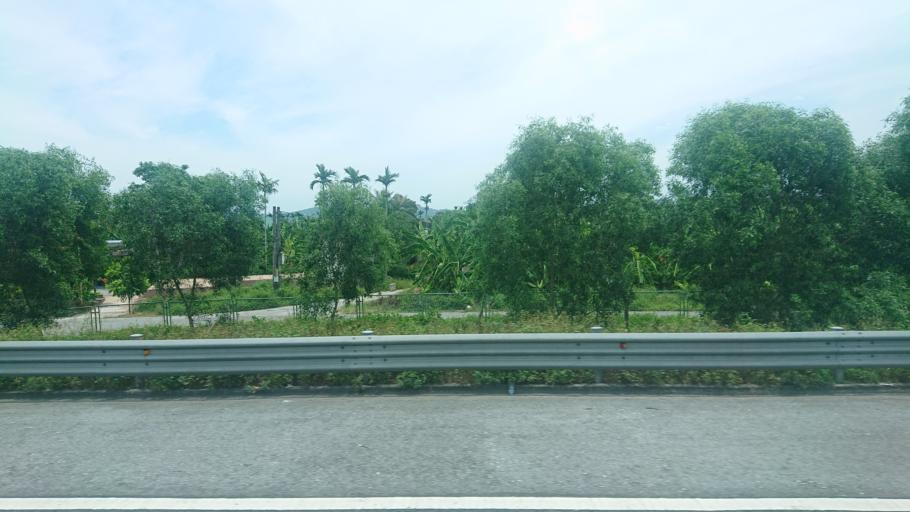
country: VN
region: Hai Phong
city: An Lao
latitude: 20.7840
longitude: 106.5639
